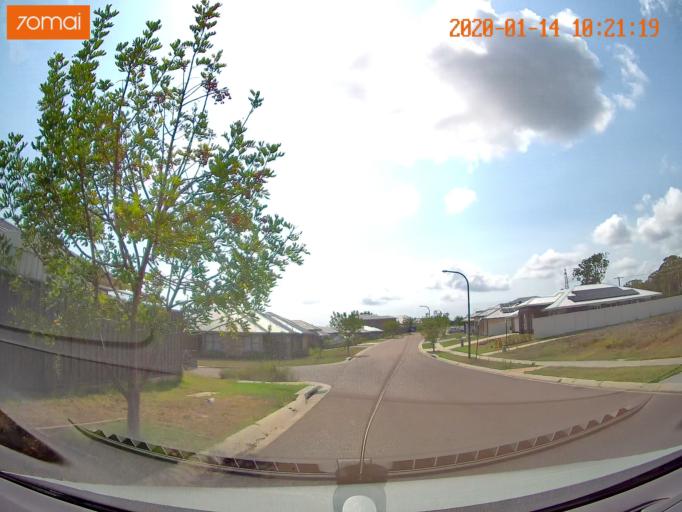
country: AU
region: New South Wales
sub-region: Lake Macquarie Shire
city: Dora Creek
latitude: -33.1099
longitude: 151.5072
